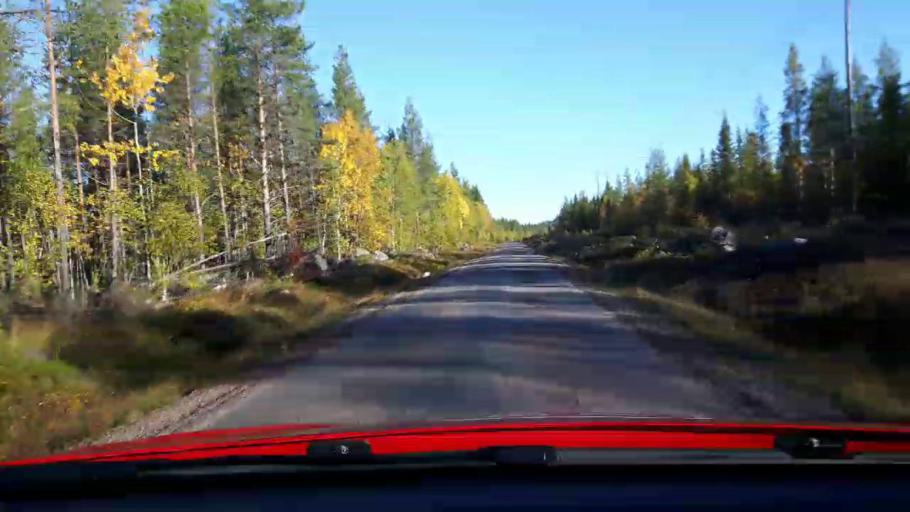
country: SE
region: Jaemtland
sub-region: Stroemsunds Kommun
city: Stroemsund
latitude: 64.3876
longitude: 15.1515
